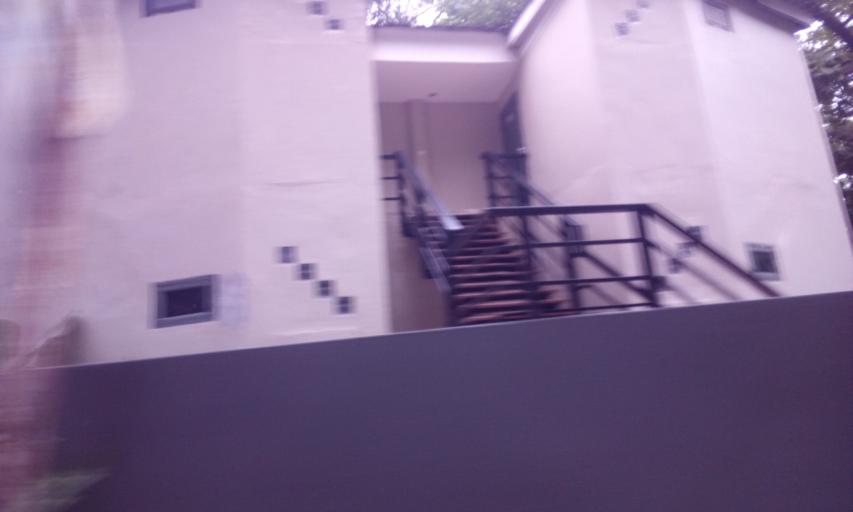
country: TH
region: Trat
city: Ko Chang Tai
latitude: 12.0087
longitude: 102.2931
